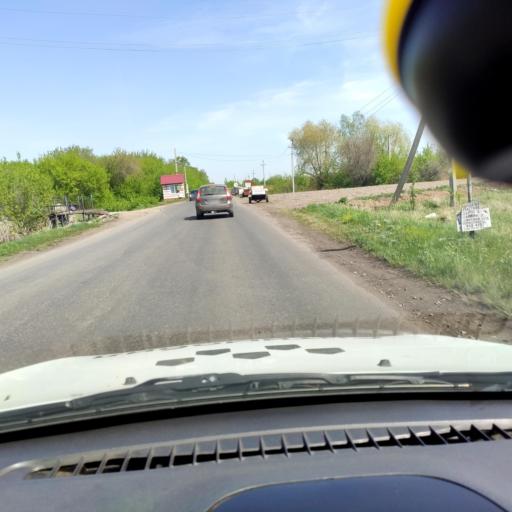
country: RU
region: Samara
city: Tol'yatti
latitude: 53.6588
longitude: 49.3325
